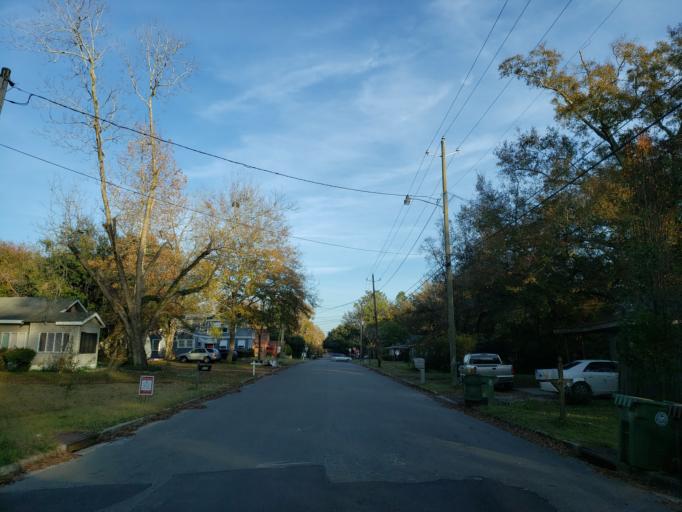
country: US
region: Mississippi
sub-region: Forrest County
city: Hattiesburg
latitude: 31.3302
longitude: -89.3052
